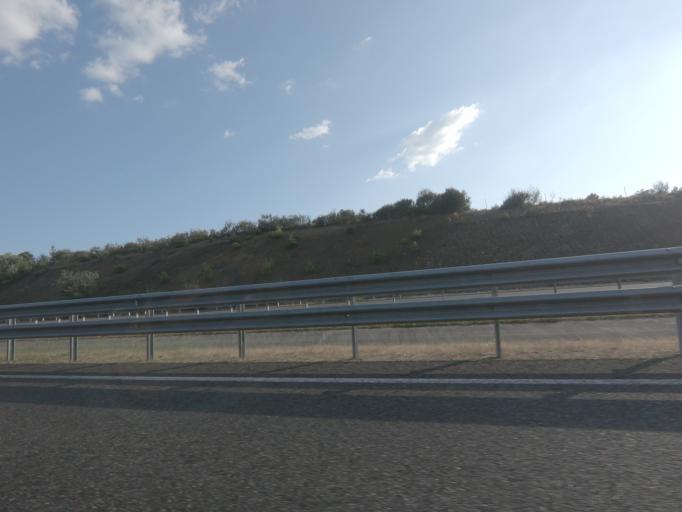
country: ES
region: Galicia
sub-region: Provincia de Ourense
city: Verin
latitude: 41.9032
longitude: -7.4276
